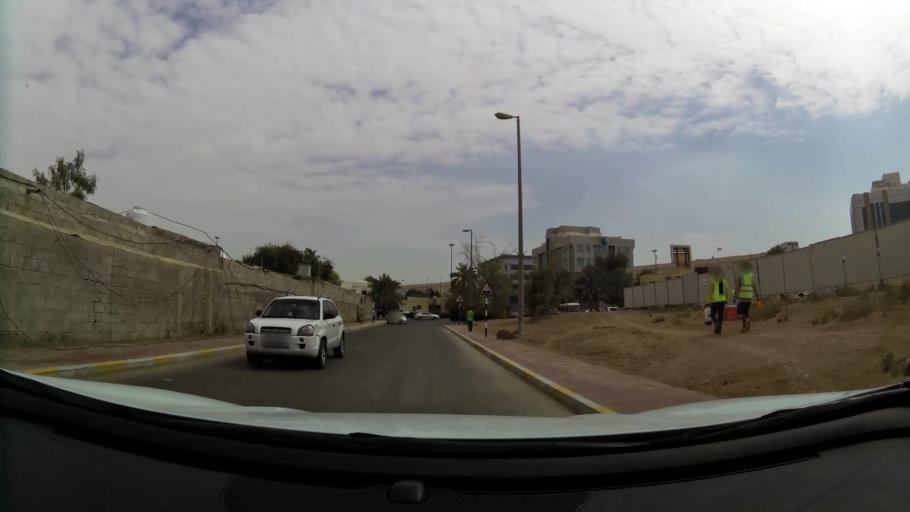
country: OM
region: Al Buraimi
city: Al Buraymi
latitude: 24.2233
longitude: 55.7790
